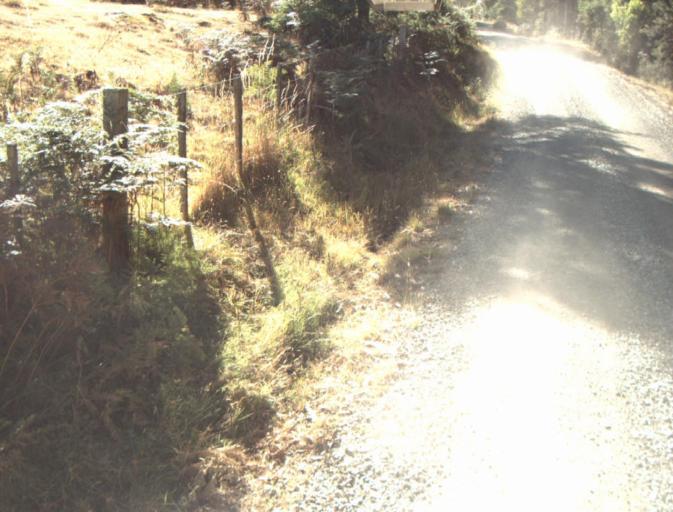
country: AU
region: Tasmania
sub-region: Launceston
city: Mayfield
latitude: -41.2898
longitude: 147.1983
